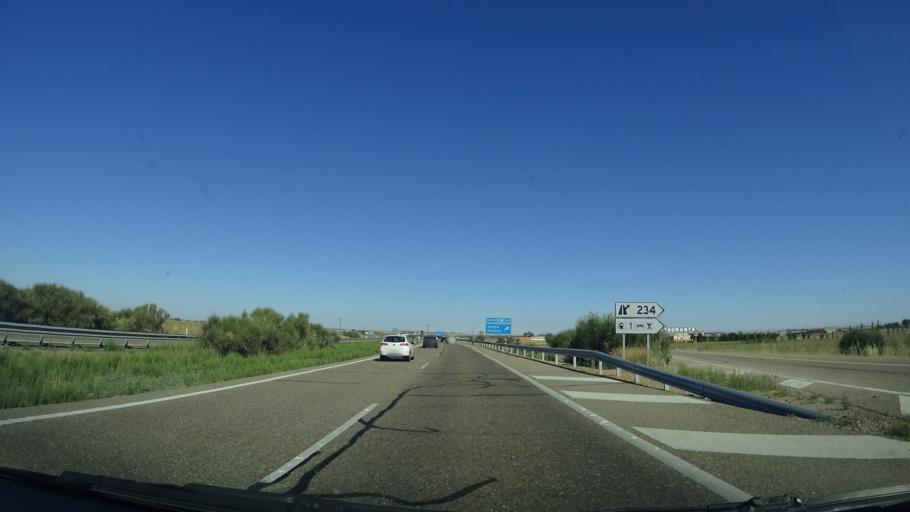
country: ES
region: Castille and Leon
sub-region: Provincia de Zamora
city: Villalpando
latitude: 41.8507
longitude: -5.4041
